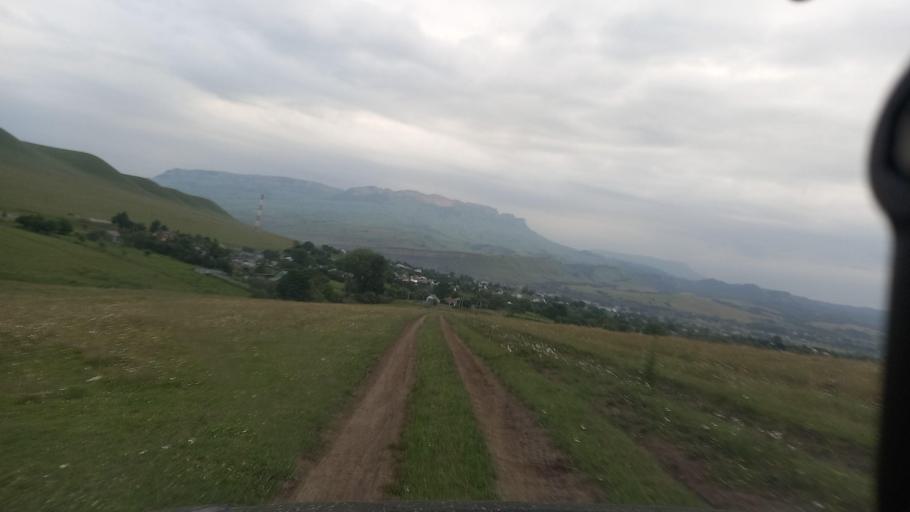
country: RU
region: Karachayevo-Cherkesiya
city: Pregradnaya
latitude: 43.9492
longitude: 41.1670
